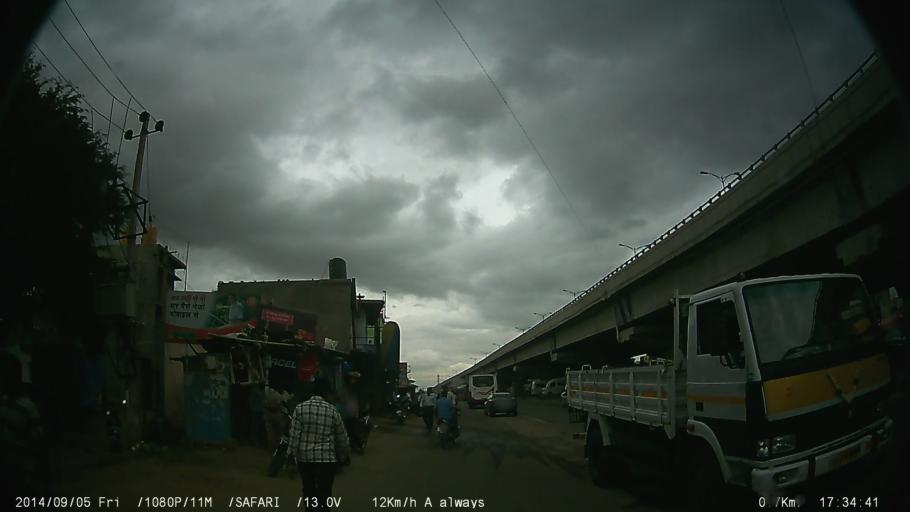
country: IN
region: Karnataka
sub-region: Bangalore Urban
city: Anekal
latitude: 12.8029
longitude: 77.7034
